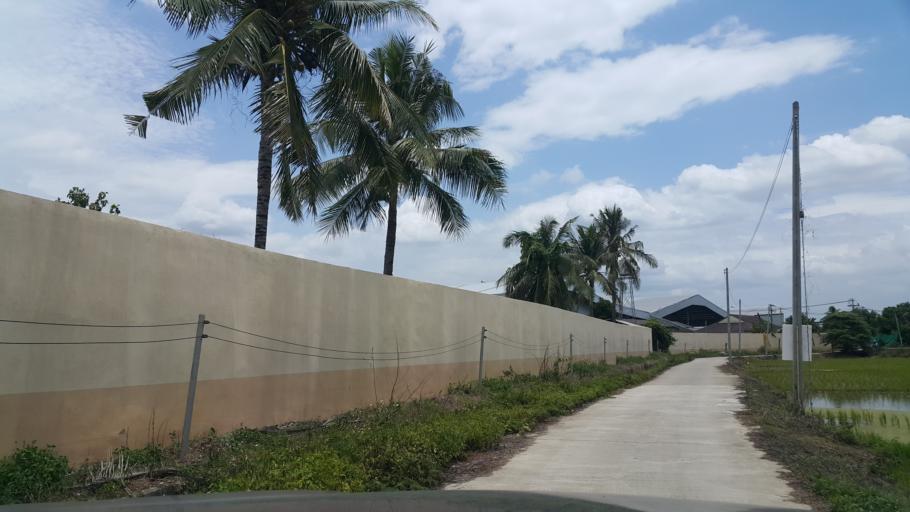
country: TH
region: Chiang Mai
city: Saraphi
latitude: 18.7307
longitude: 98.9941
